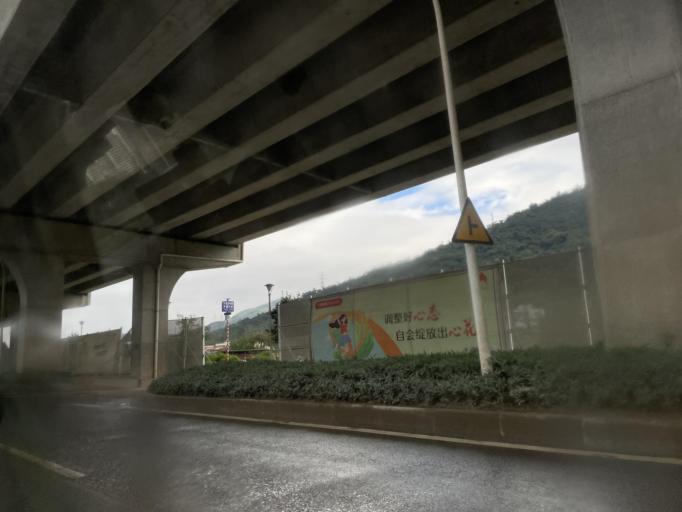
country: CN
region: Guangdong
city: Nanping
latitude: 22.1834
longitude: 113.4625
